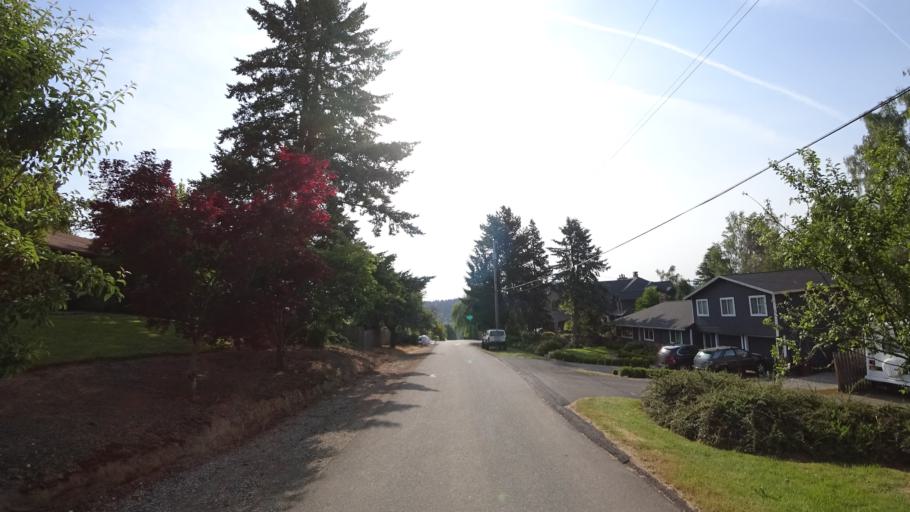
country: US
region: Oregon
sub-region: Clackamas County
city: Happy Valley
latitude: 45.4512
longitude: -122.5341
